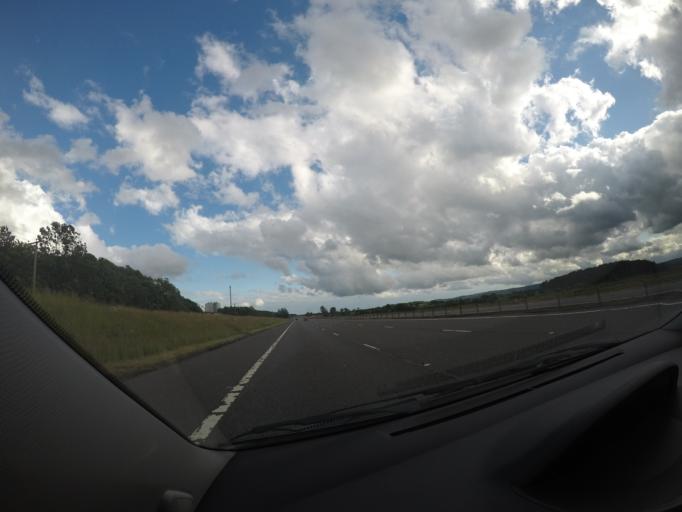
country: GB
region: Scotland
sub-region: Dumfries and Galloway
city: Lockerbie
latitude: 55.1587
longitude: -3.3853
